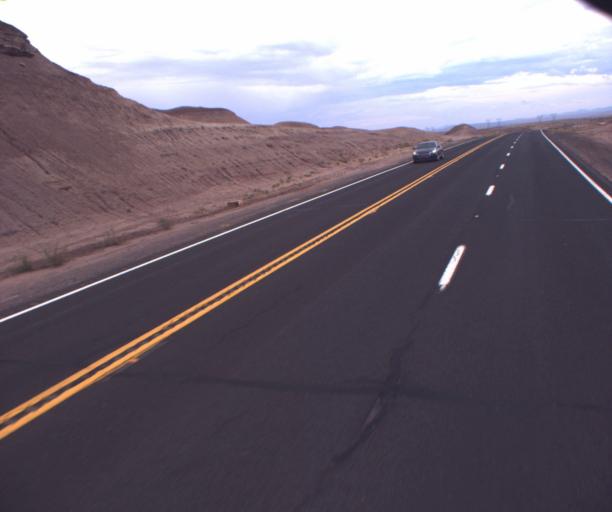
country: US
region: Arizona
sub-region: Coconino County
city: Tuba City
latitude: 35.9955
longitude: -111.3929
